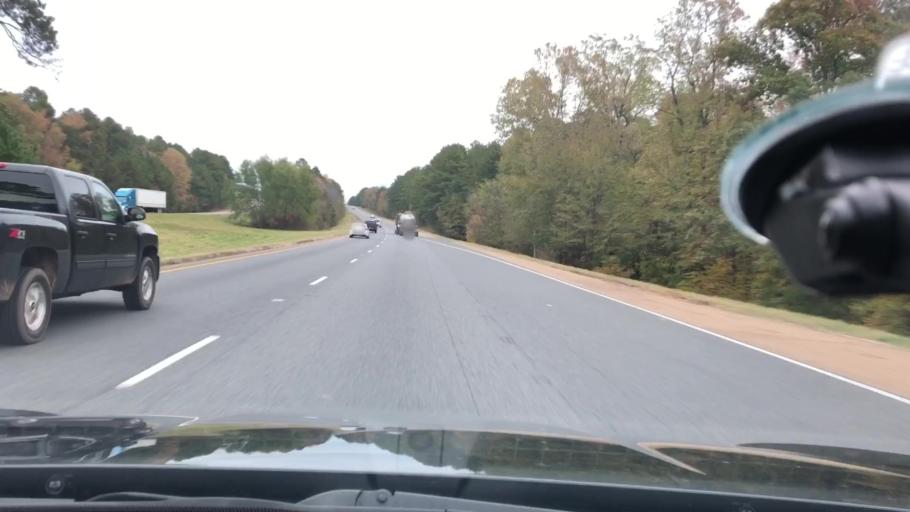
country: US
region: Arkansas
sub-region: Clark County
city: Gurdon
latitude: 33.9319
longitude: -93.2567
